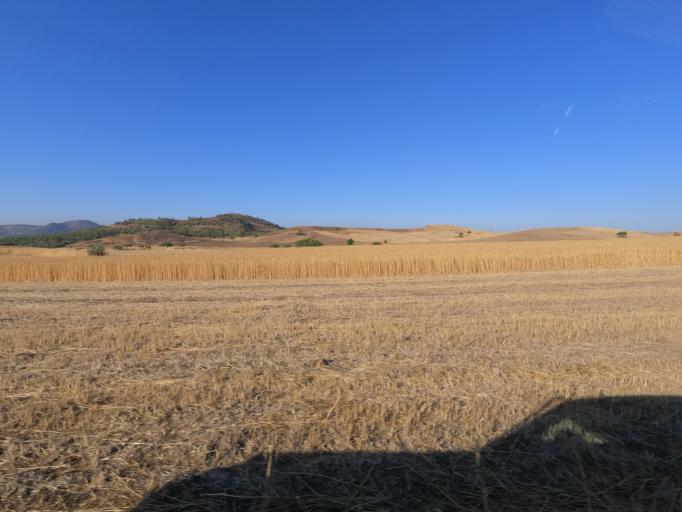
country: CY
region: Larnaka
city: Troulloi
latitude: 35.0253
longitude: 33.6349
